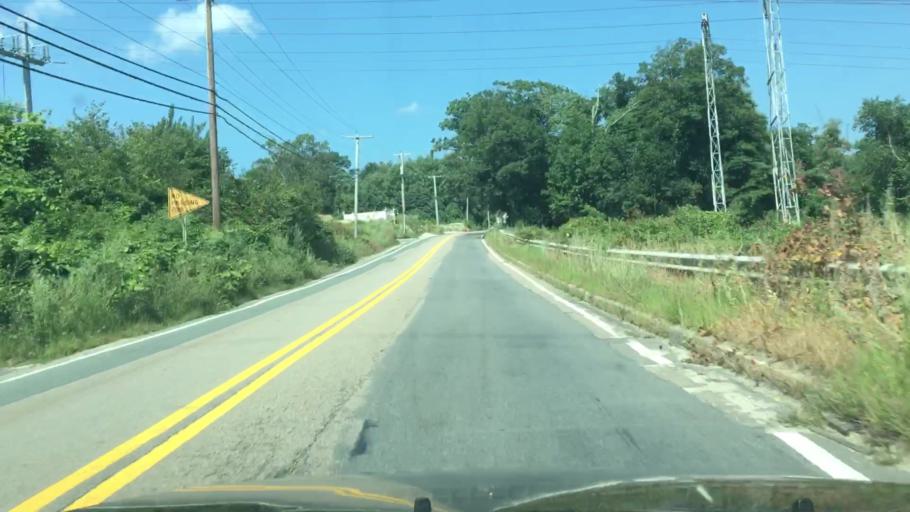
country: US
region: Massachusetts
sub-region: Worcester County
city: Milford
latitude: 42.1571
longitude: -71.4863
